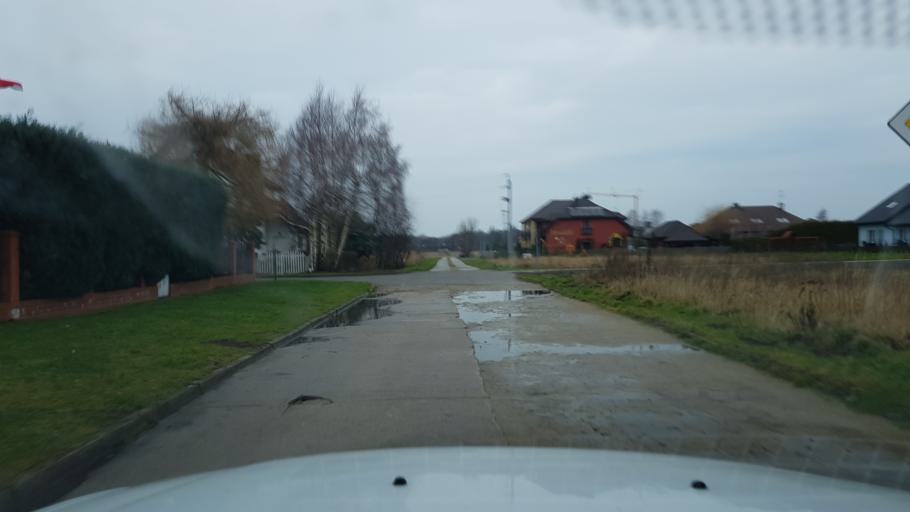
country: PL
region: West Pomeranian Voivodeship
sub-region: Powiat kolobrzeski
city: Grzybowo
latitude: 54.1603
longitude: 15.4895
